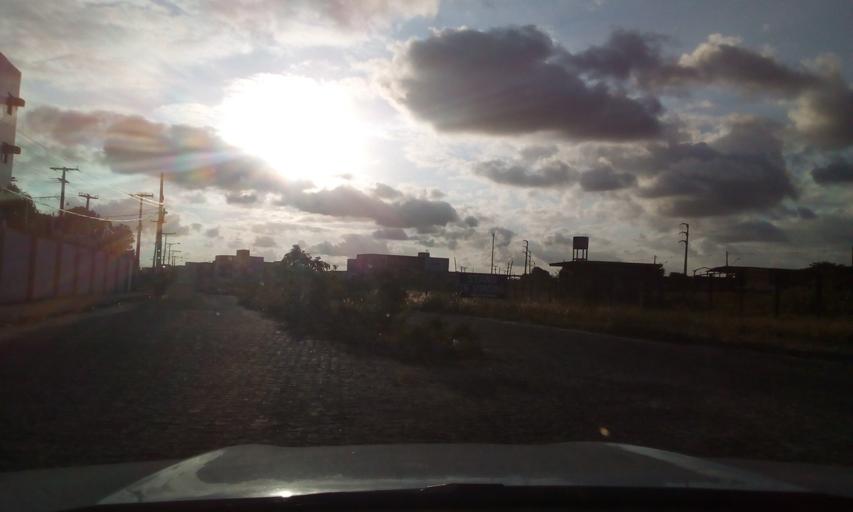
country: BR
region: Paraiba
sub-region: Joao Pessoa
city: Joao Pessoa
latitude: -7.1861
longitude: -34.8770
